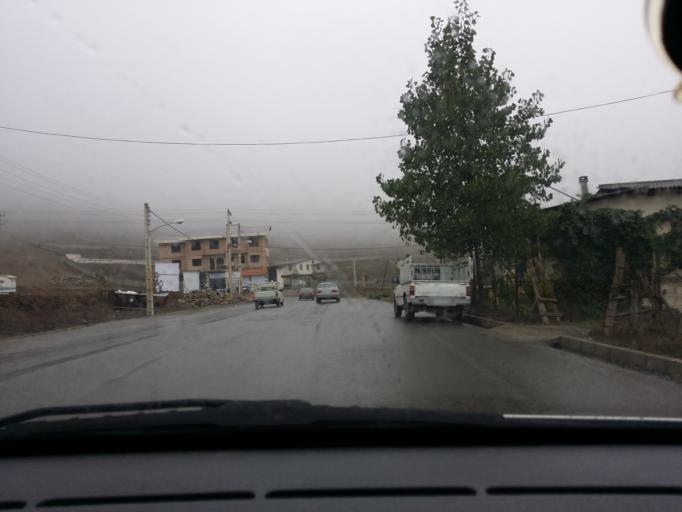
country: IR
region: Mazandaran
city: Chalus
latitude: 36.5210
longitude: 51.2357
